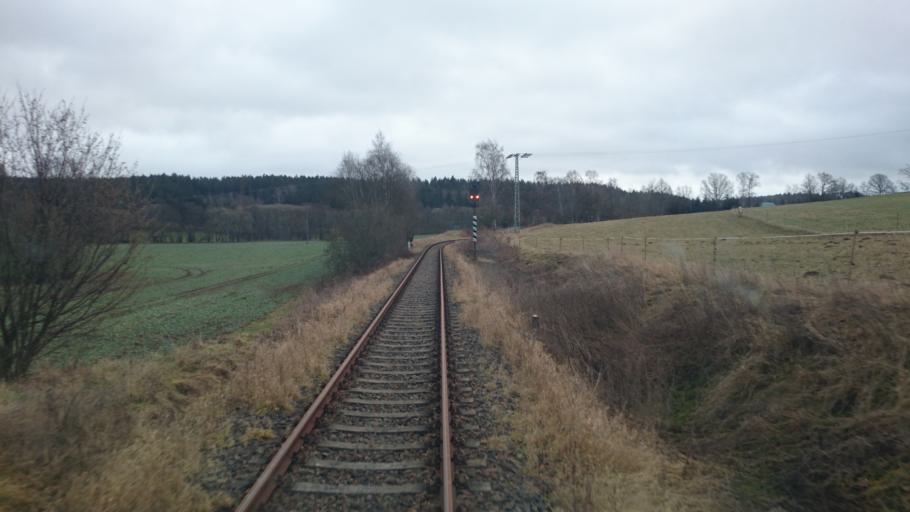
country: DE
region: Thuringia
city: Lohma
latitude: 50.5829
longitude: 11.8444
